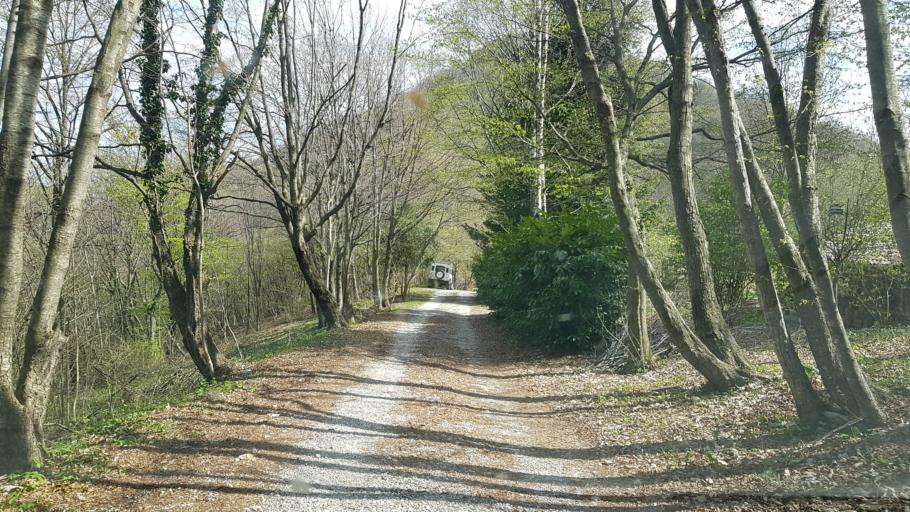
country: IT
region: Friuli Venezia Giulia
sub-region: Provincia di Udine
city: Trasaghis
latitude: 46.2857
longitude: 13.0402
